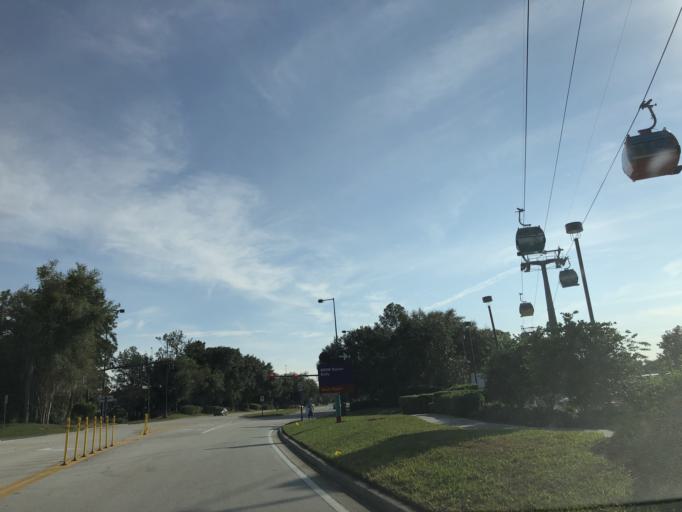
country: US
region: Florida
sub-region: Osceola County
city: Celebration
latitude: 28.3666
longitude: -81.5539
